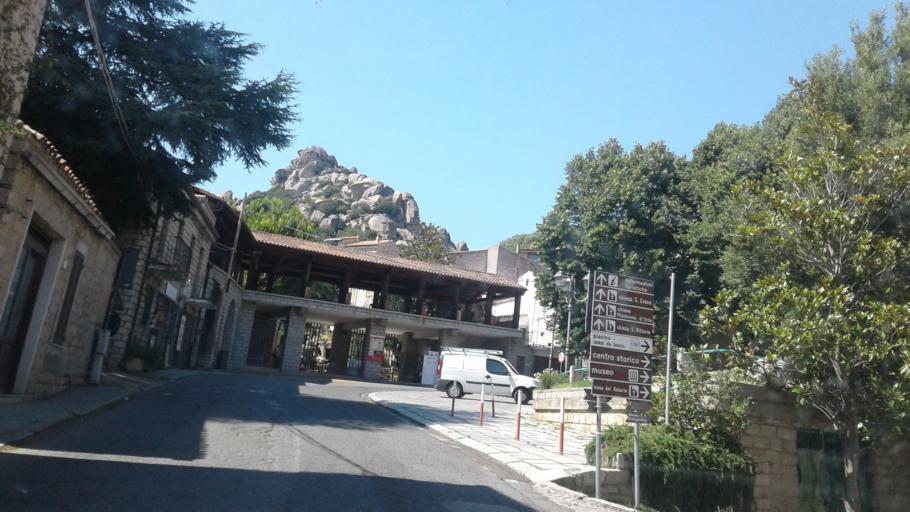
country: IT
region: Sardinia
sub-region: Provincia di Olbia-Tempio
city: Aggius
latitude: 40.9279
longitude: 9.0635
